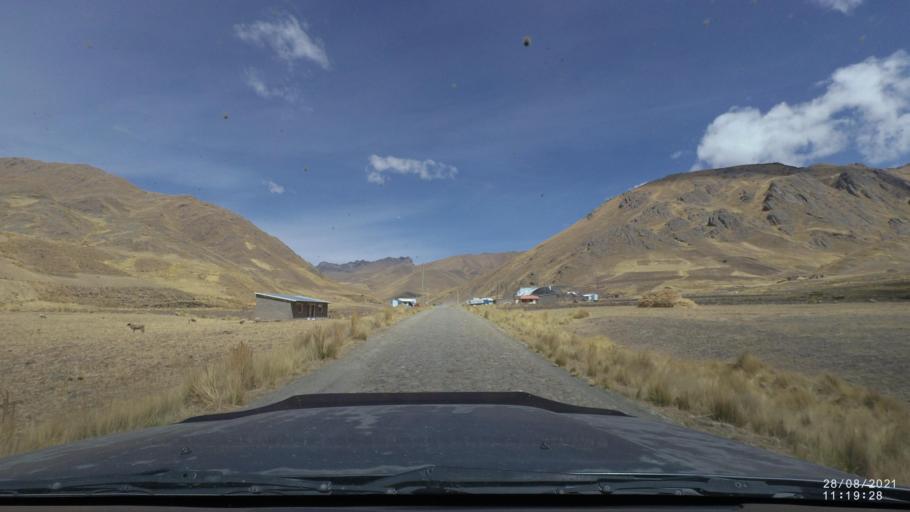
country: BO
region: Cochabamba
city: Cochabamba
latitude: -17.1538
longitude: -66.3328
